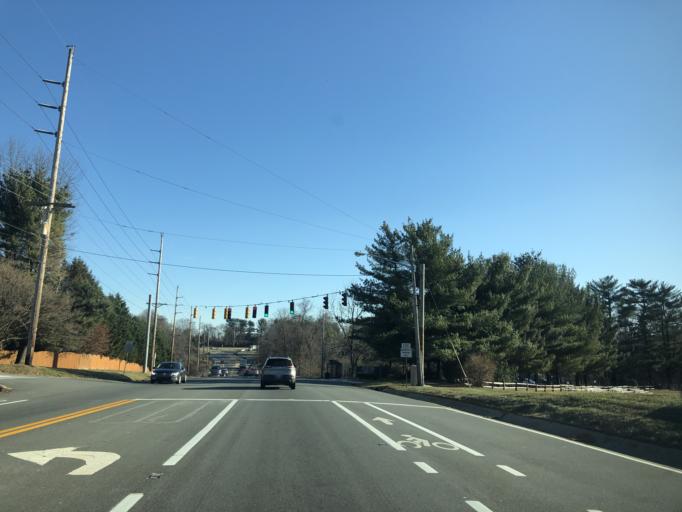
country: US
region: Delaware
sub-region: New Castle County
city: Hockessin
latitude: 39.7757
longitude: -75.6751
